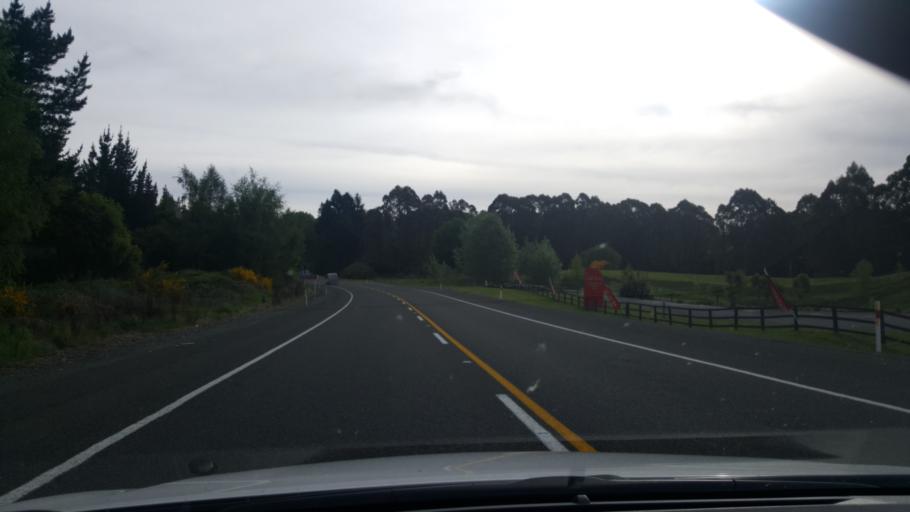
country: NZ
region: Waikato
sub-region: Taupo District
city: Taupo
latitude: -38.6153
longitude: 176.1134
